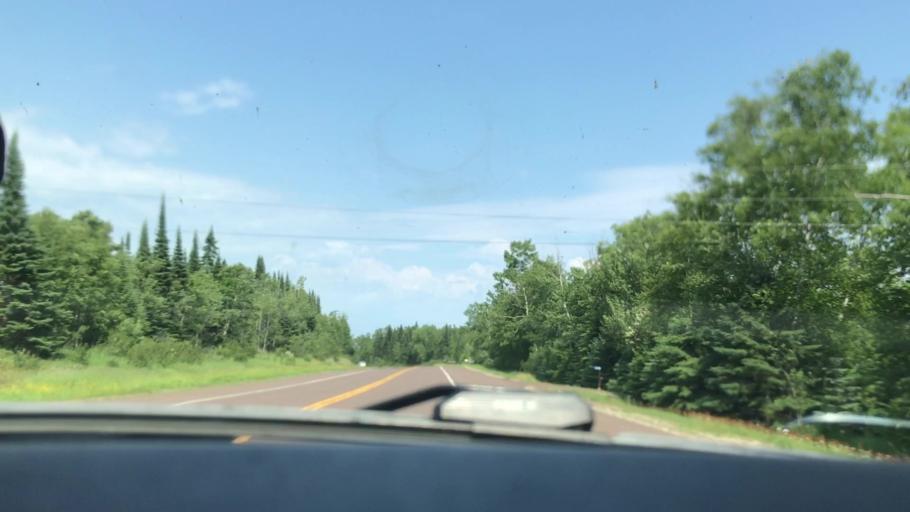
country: US
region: Minnesota
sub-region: Cook County
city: Grand Marais
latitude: 47.7773
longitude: -90.1950
